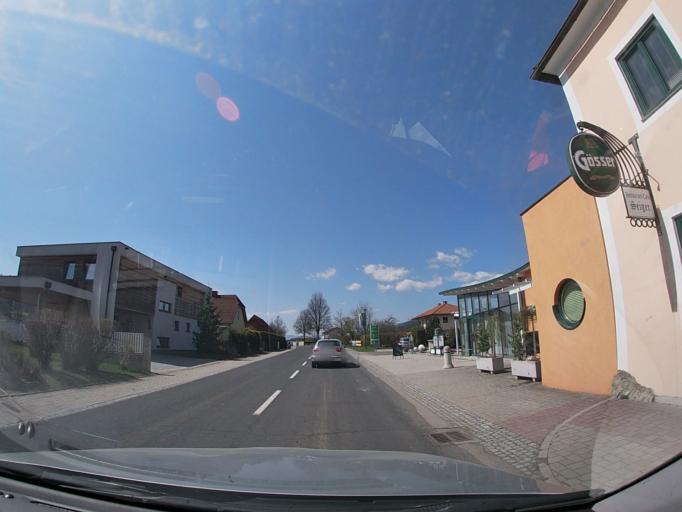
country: AT
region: Styria
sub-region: Politischer Bezirk Murtal
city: Sankt Lorenzen bei Knittelfeld
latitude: 47.2495
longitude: 14.8943
